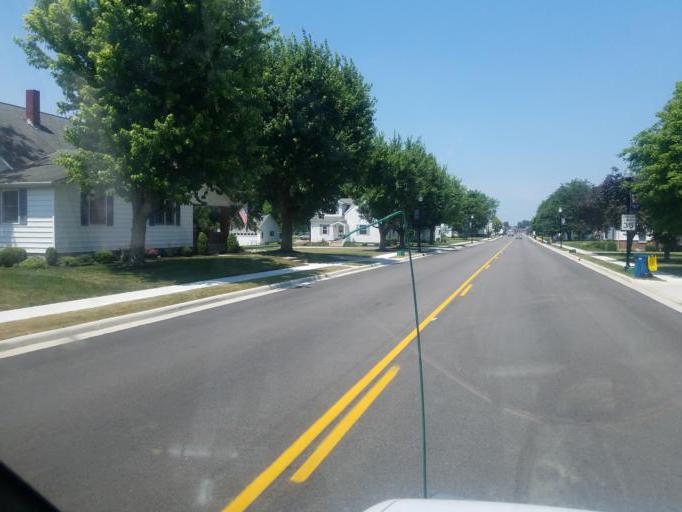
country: US
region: Ohio
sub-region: Shelby County
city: Fort Loramie
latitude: 40.3433
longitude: -84.3752
